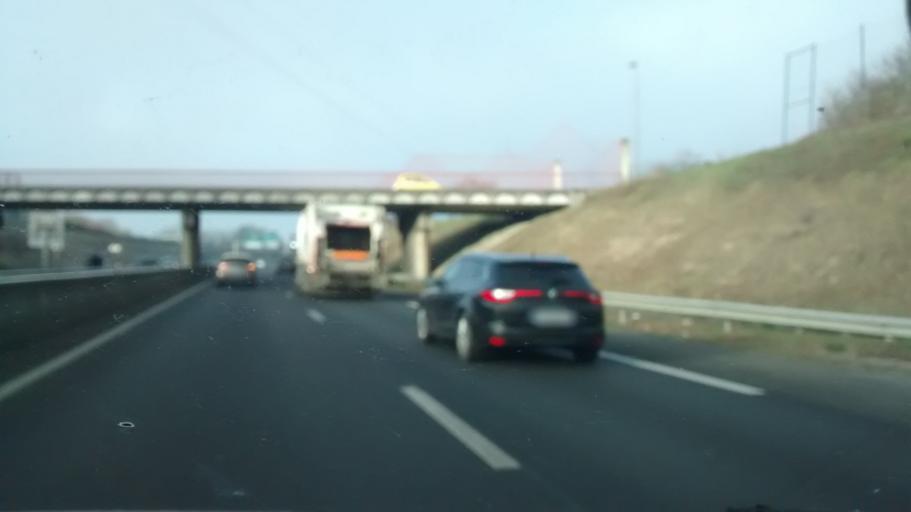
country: FR
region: Centre
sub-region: Departement d'Indre-et-Loire
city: Joue-les-Tours
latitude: 47.3409
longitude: 0.6554
